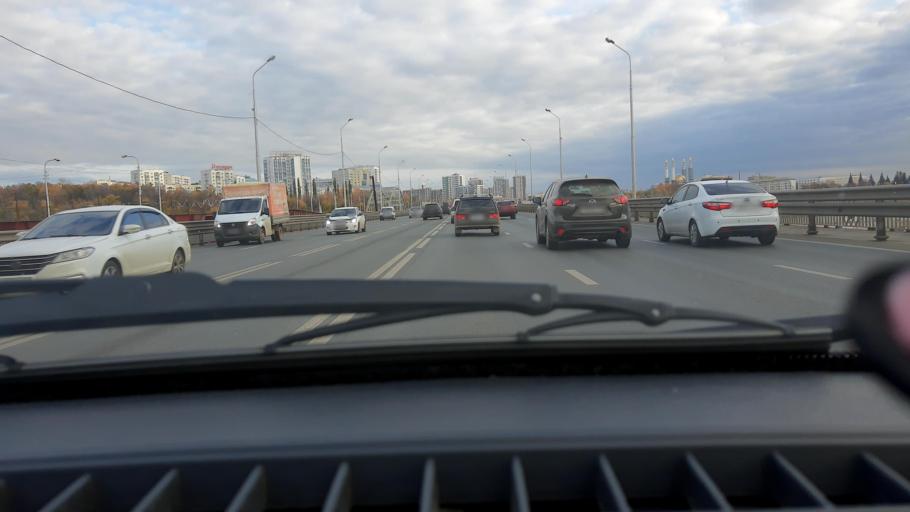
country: RU
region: Bashkortostan
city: Ufa
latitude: 54.7041
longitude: 55.9544
